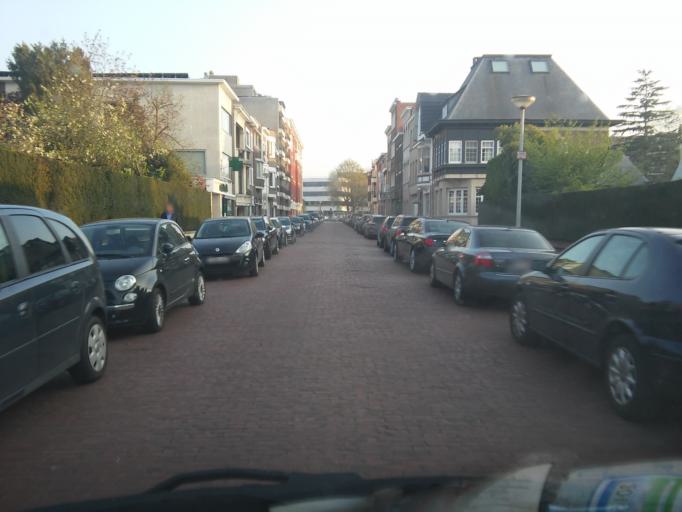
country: BE
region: Flanders
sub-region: Provincie Antwerpen
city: Antwerpen
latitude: 51.1762
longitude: 4.4026
